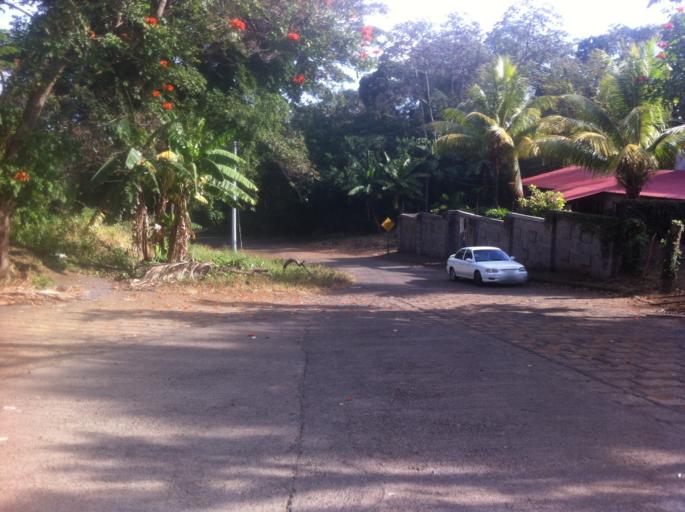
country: NI
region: Managua
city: El Crucero
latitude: 12.0551
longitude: -86.3326
